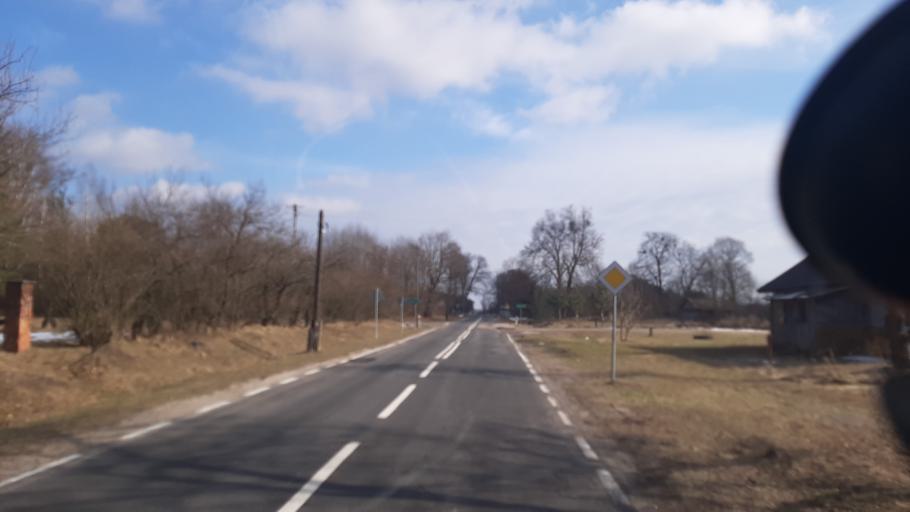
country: PL
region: Lublin Voivodeship
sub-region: Powiat wlodawski
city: Urszulin
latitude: 51.4968
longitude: 23.2122
